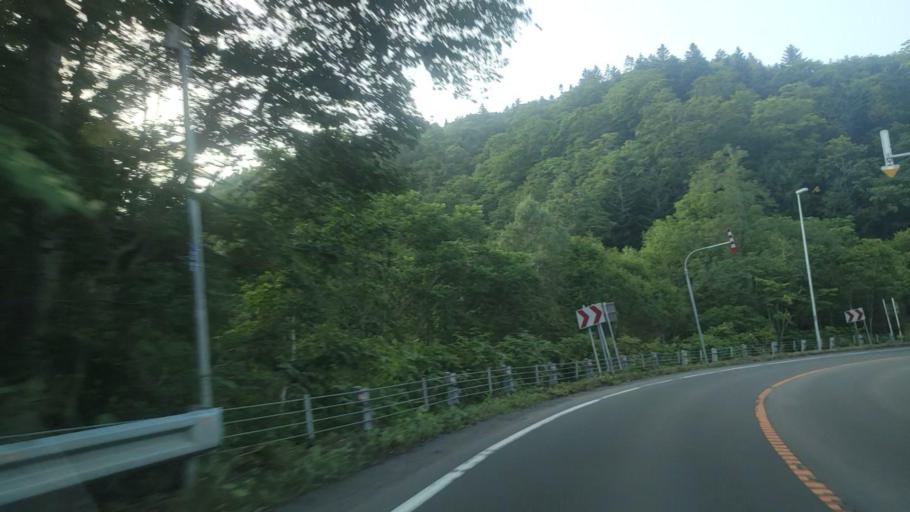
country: JP
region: Hokkaido
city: Bibai
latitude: 43.2584
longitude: 142.0270
